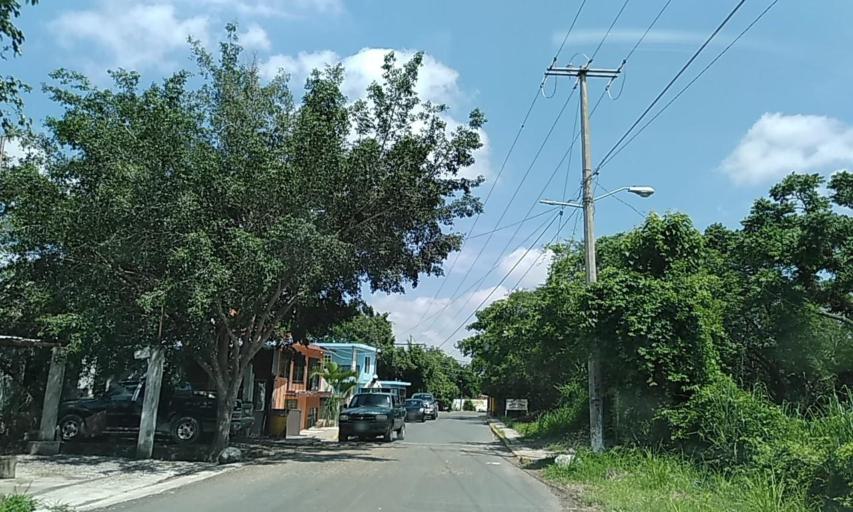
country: MX
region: Veracruz
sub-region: Emiliano Zapata
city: Dos Rios
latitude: 19.4381
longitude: -96.7790
